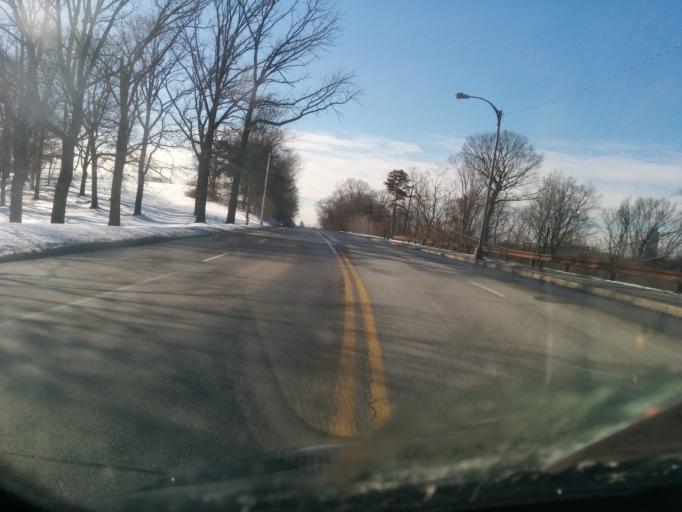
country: US
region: Pennsylvania
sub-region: Allegheny County
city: Bloomfield
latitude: 40.4338
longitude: -79.9379
